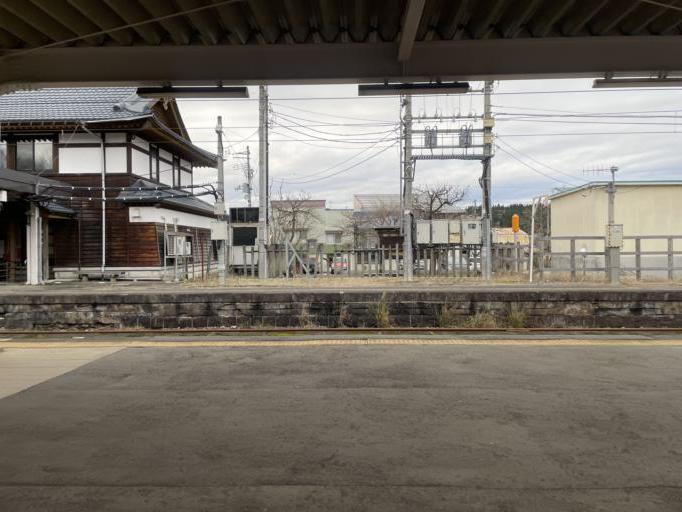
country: JP
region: Yamagata
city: Shinjo
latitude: 38.8583
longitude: 140.2550
